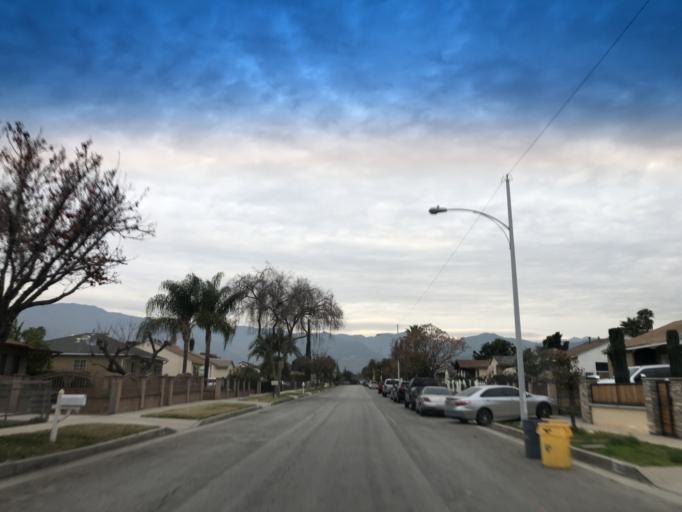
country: US
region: California
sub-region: Los Angeles County
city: Azusa
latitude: 34.1188
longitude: -117.9140
